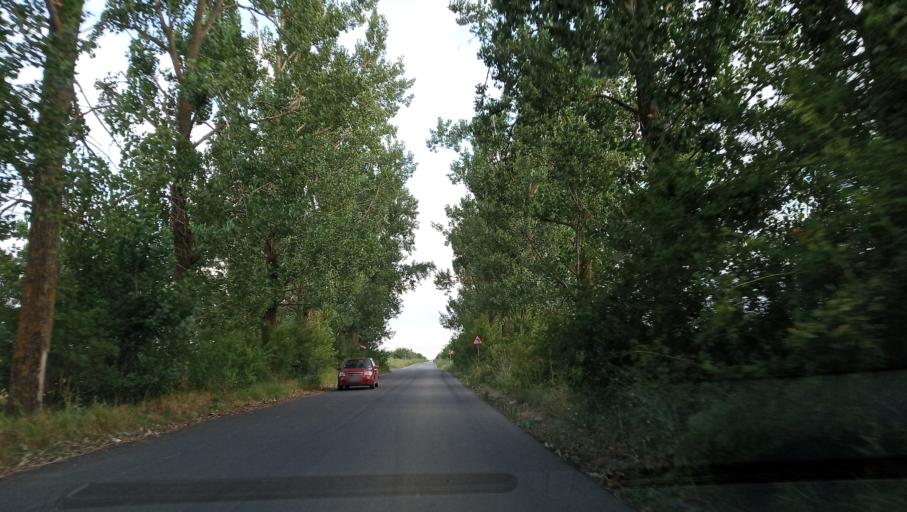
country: RO
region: Giurgiu
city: Gostinari-Vacaresti
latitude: 44.1731
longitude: 26.2095
